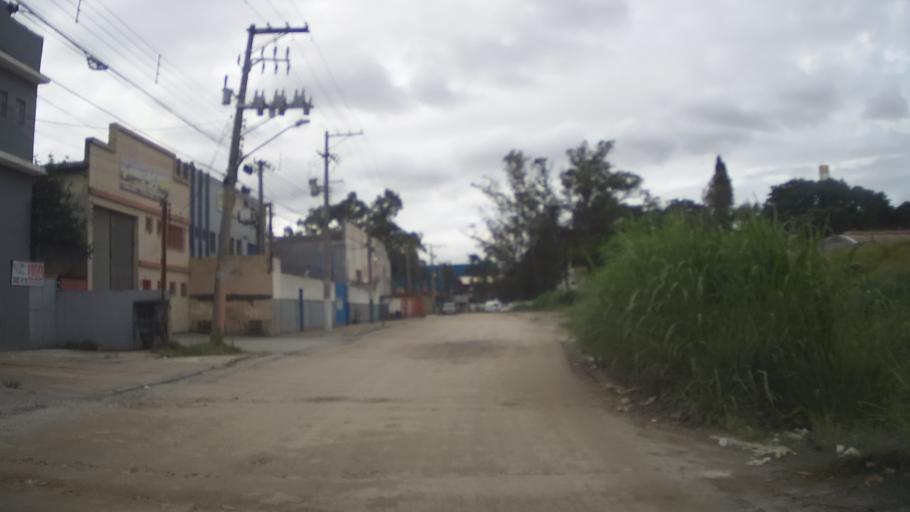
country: BR
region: Sao Paulo
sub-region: Guarulhos
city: Guarulhos
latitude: -23.4665
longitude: -46.4639
